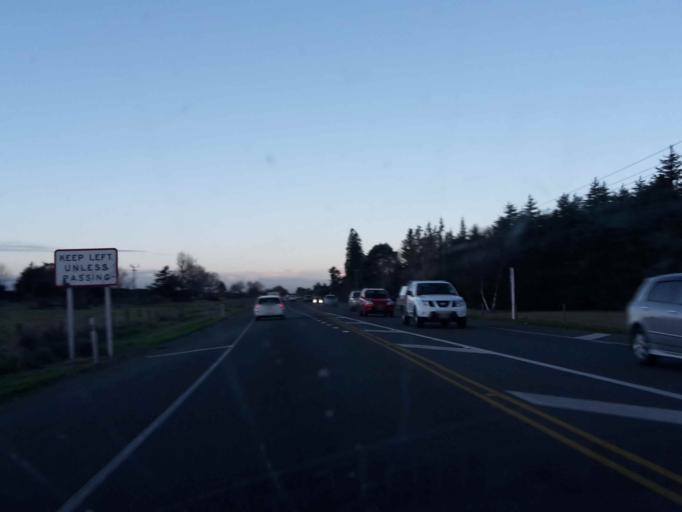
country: NZ
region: Canterbury
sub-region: Selwyn District
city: Prebbleton
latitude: -43.5606
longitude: 172.4596
